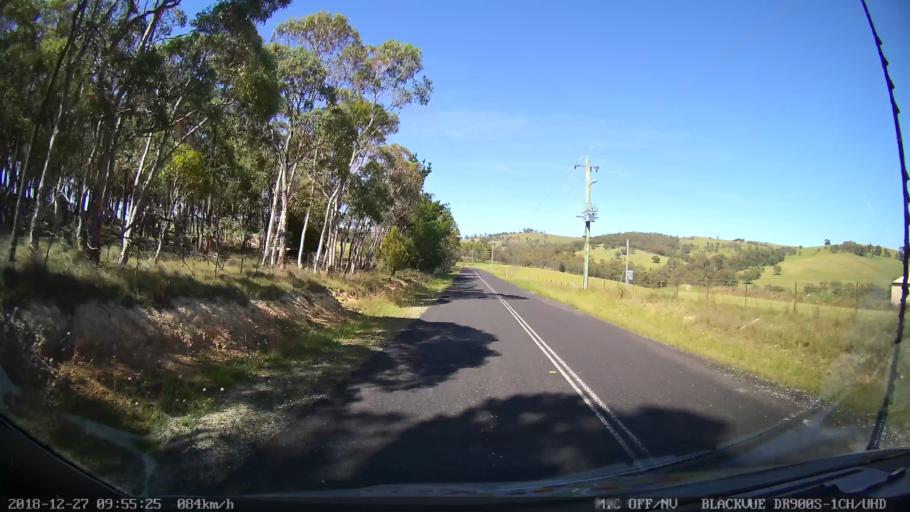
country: AU
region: New South Wales
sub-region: Lithgow
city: Portland
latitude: -33.4014
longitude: 149.9758
